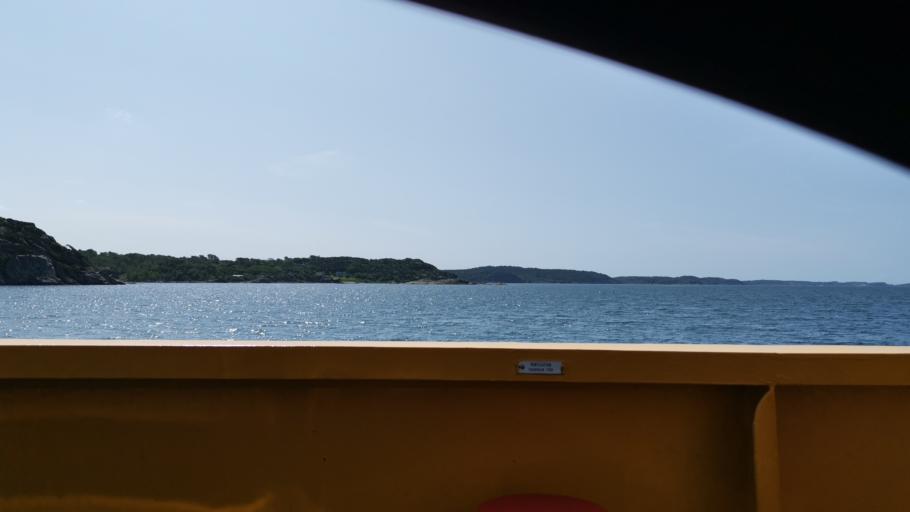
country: SE
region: Vaestra Goetaland
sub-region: Lysekils Kommun
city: Brastad
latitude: 58.3030
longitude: 11.5288
